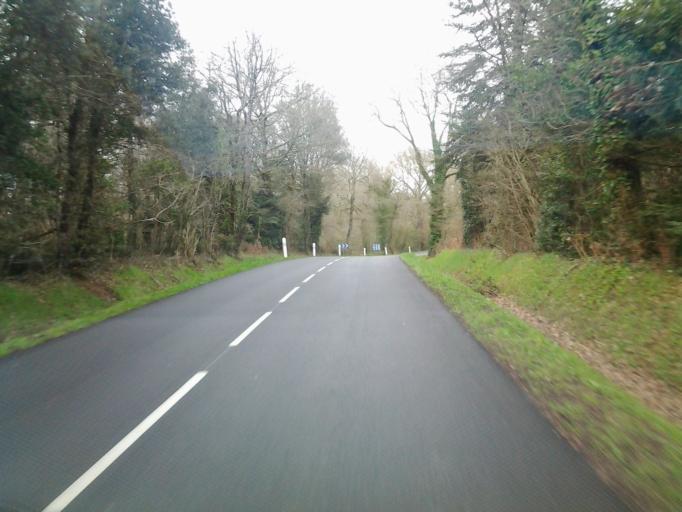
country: FR
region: Pays de la Loire
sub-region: Departement de la Vendee
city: Avrille
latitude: 46.4864
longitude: -1.4683
